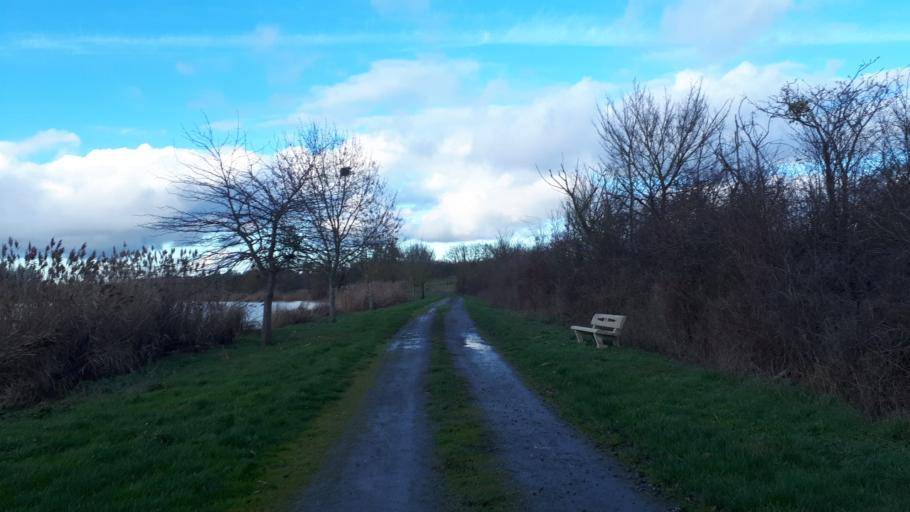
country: FR
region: Poitou-Charentes
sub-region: Departement de la Vienne
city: Pleumartin
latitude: 46.6343
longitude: 0.7659
